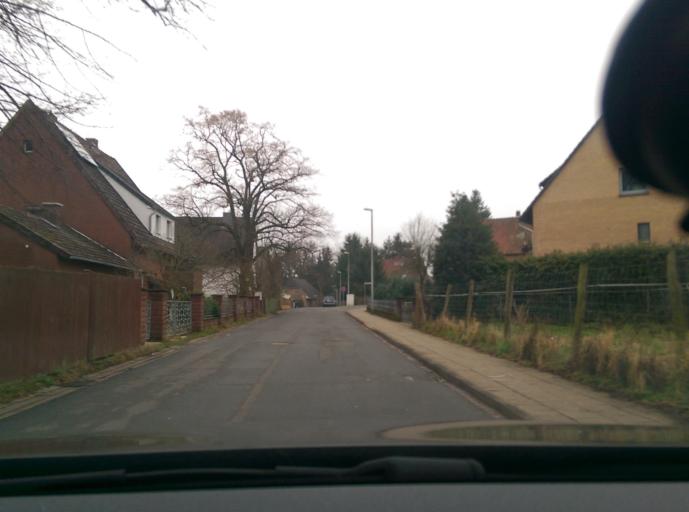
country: DE
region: Lower Saxony
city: Elze
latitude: 52.5459
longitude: 9.7428
